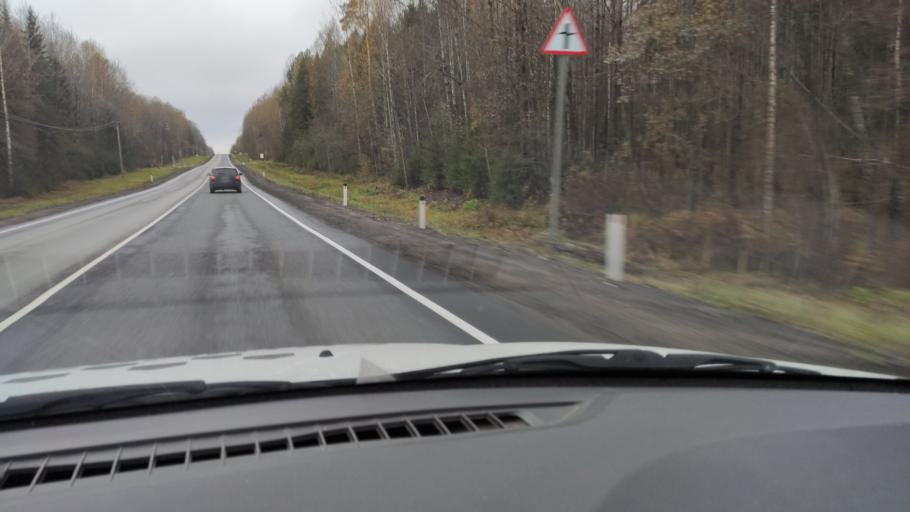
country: RU
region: Kirov
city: Belaya Kholunitsa
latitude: 58.9195
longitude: 51.1080
